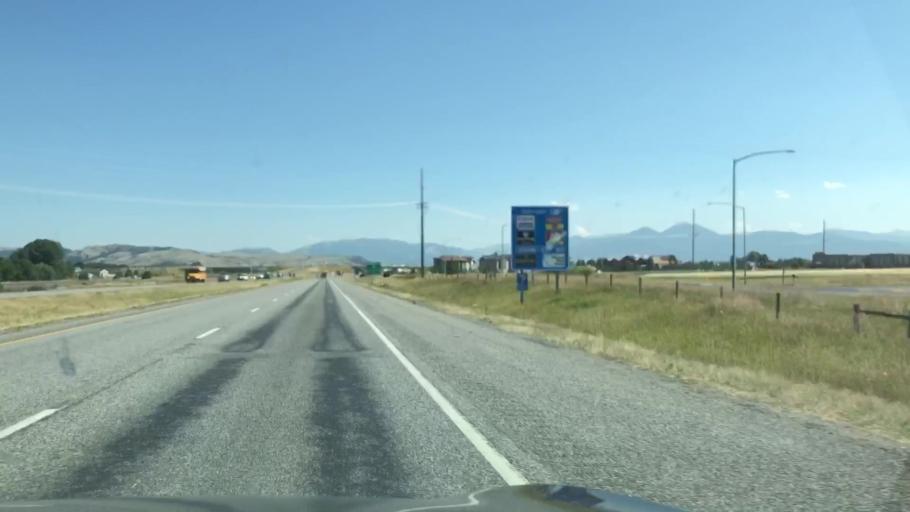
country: US
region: Montana
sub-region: Gallatin County
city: Bozeman
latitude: 45.7209
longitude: -111.0737
